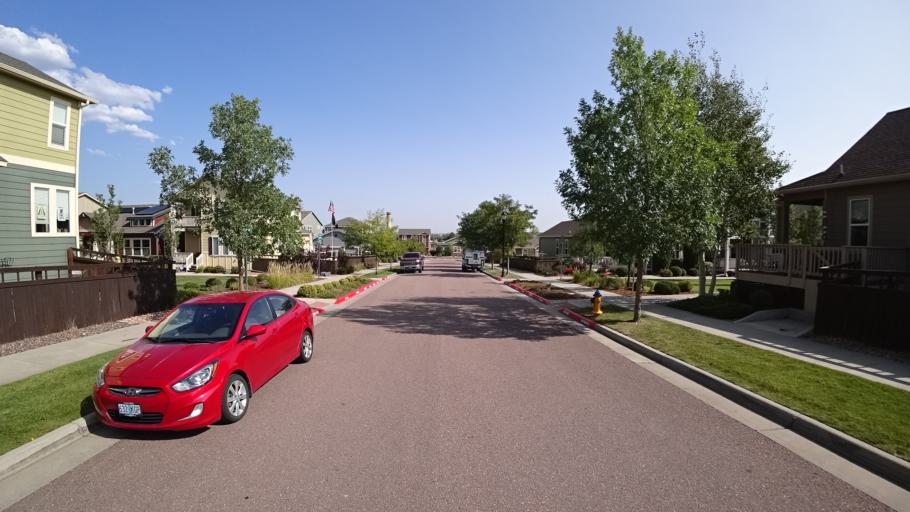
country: US
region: Colorado
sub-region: El Paso County
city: Colorado Springs
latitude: 38.8305
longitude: -104.8558
